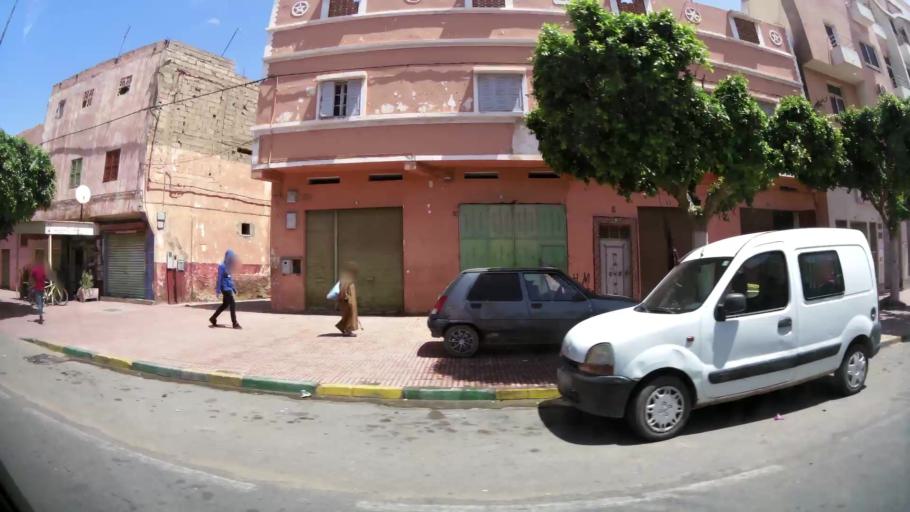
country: MA
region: Souss-Massa-Draa
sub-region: Inezgane-Ait Mellou
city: Inezgane
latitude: 30.3444
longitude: -9.4995
